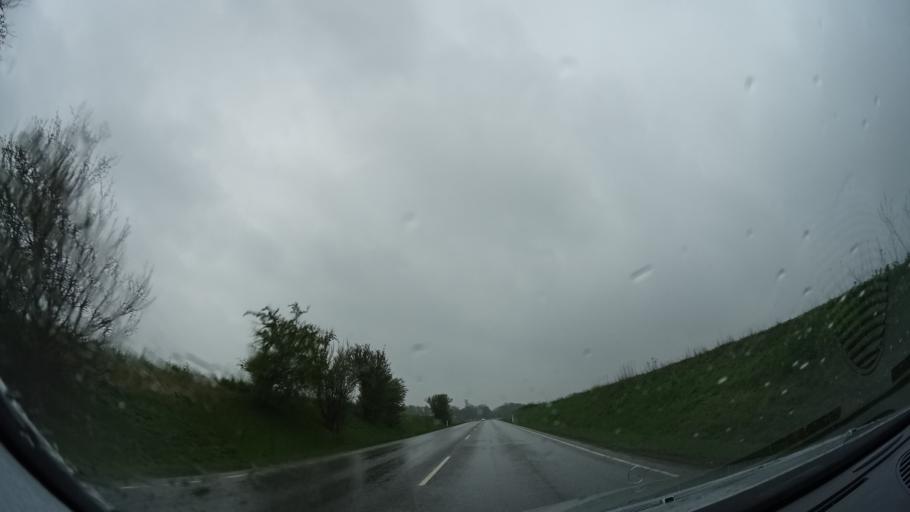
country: DK
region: Zealand
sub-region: Holbaek Kommune
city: Holbaek
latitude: 55.7524
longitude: 11.6222
